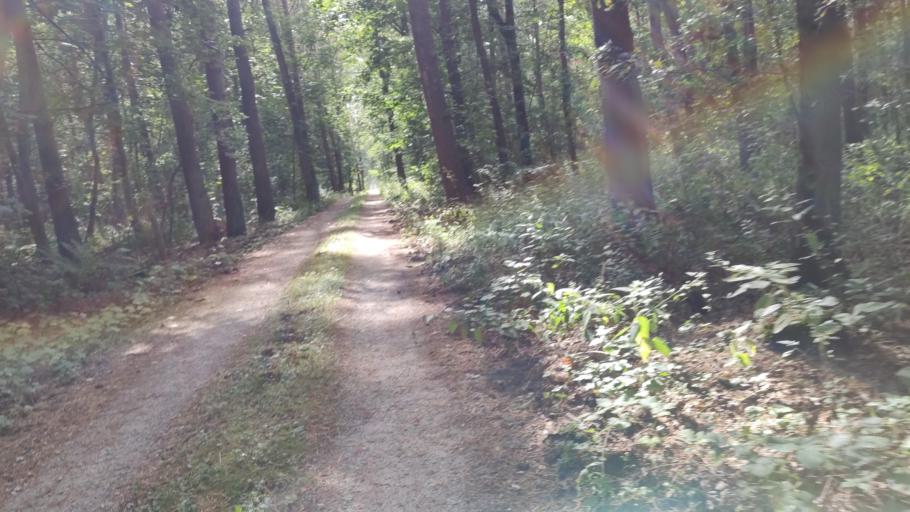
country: PL
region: Kujawsko-Pomorskie
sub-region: Powiat zninski
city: Barcin
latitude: 52.8320
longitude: 17.9419
